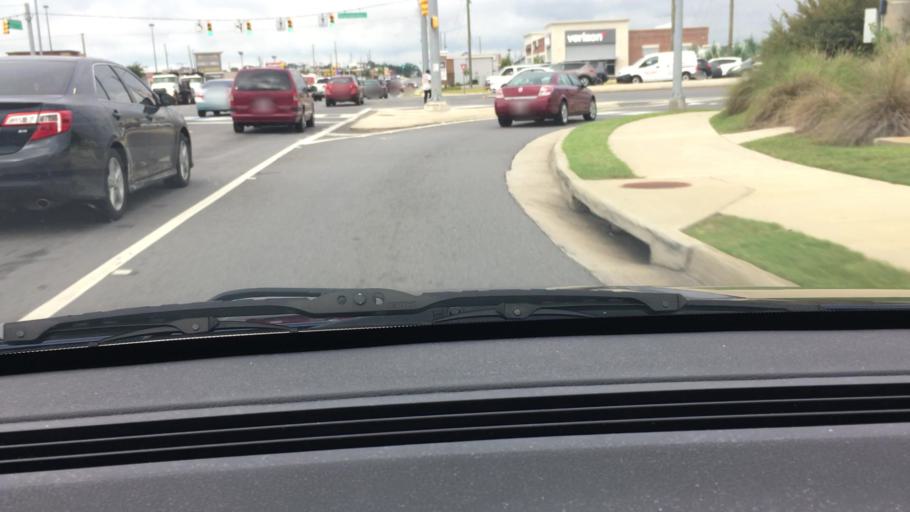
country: US
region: Alabama
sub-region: Tuscaloosa County
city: Tuscaloosa
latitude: 33.1973
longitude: -87.5252
